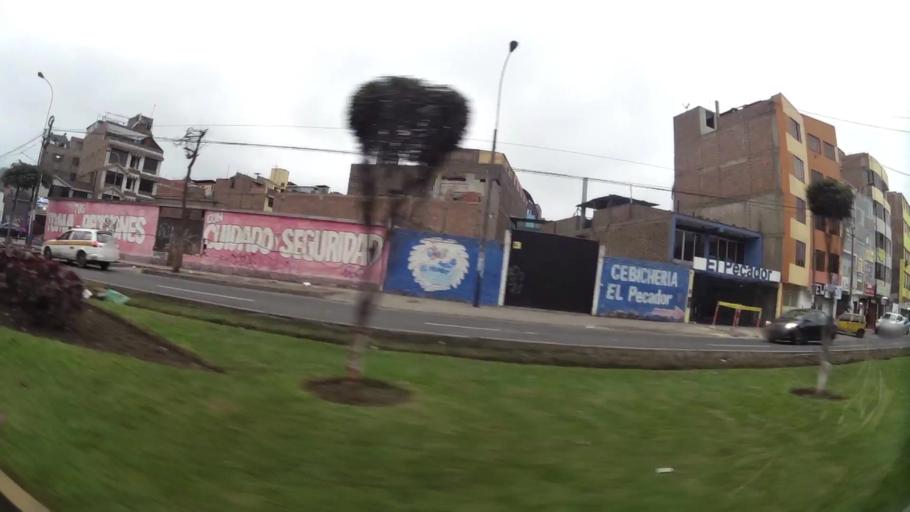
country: PE
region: Lima
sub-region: Lima
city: San Luis
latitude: -12.0748
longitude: -76.9781
